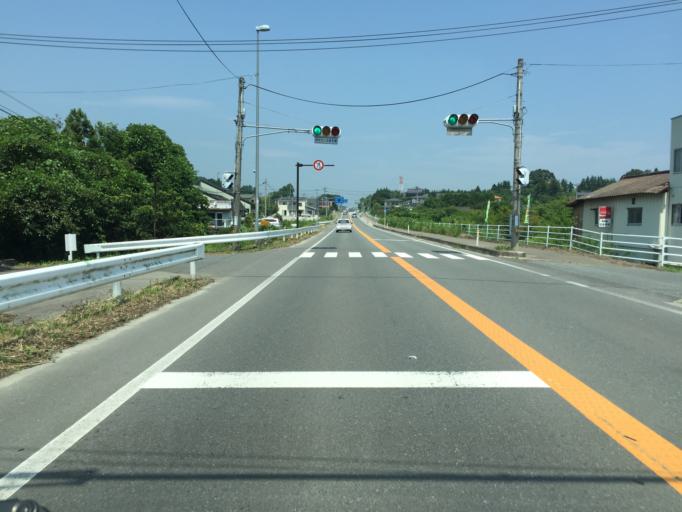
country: JP
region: Miyagi
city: Marumori
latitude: 37.8331
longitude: 140.9184
